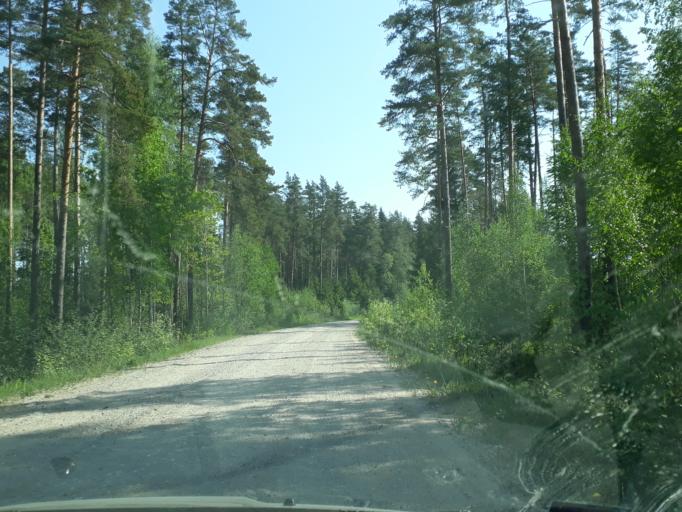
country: LV
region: Ligatne
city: Ligatne
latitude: 57.2731
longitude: 25.0375
